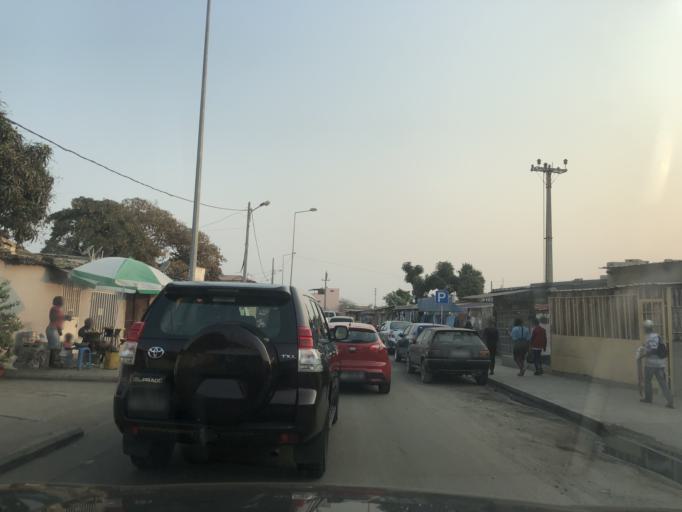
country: AO
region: Luanda
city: Luanda
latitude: -8.8424
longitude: 13.2253
